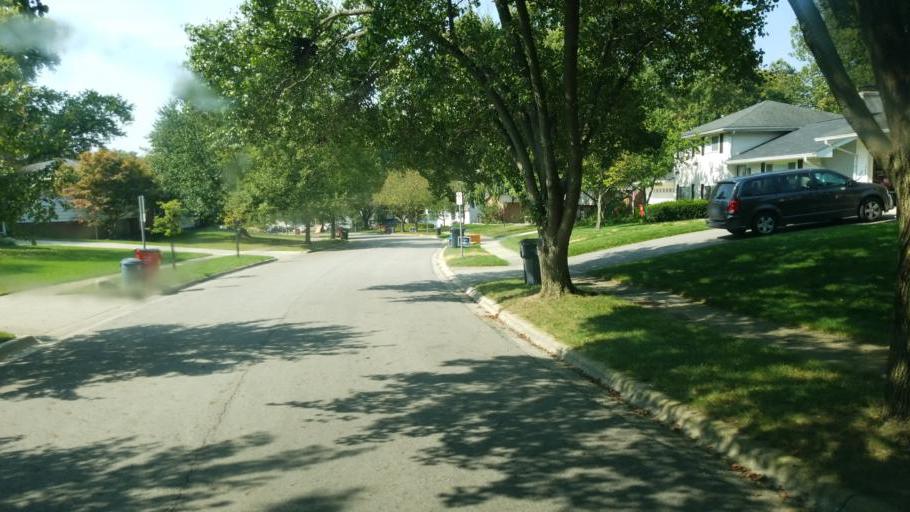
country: US
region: Ohio
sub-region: Franklin County
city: Worthington
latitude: 40.0883
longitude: -83.0276
